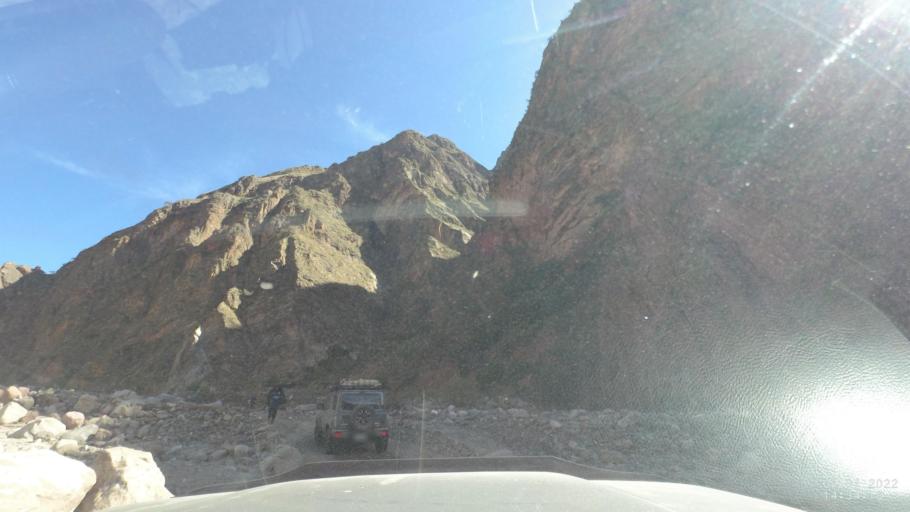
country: BO
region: Cochabamba
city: Irpa Irpa
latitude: -17.8389
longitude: -66.4168
